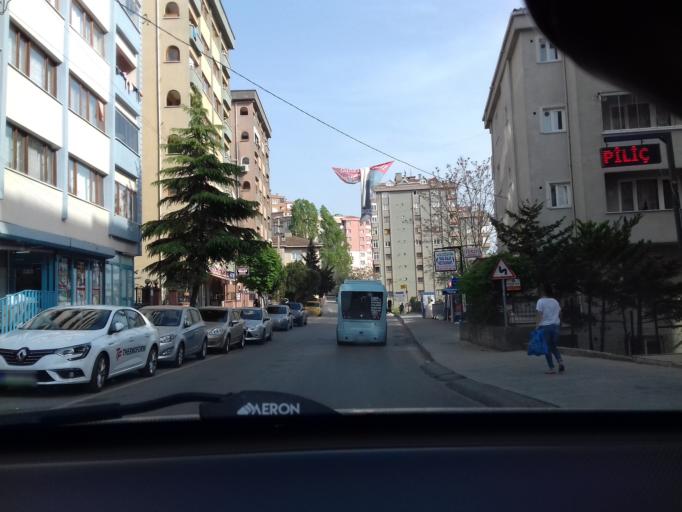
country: TR
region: Istanbul
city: Pendik
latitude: 40.9101
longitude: 29.2341
